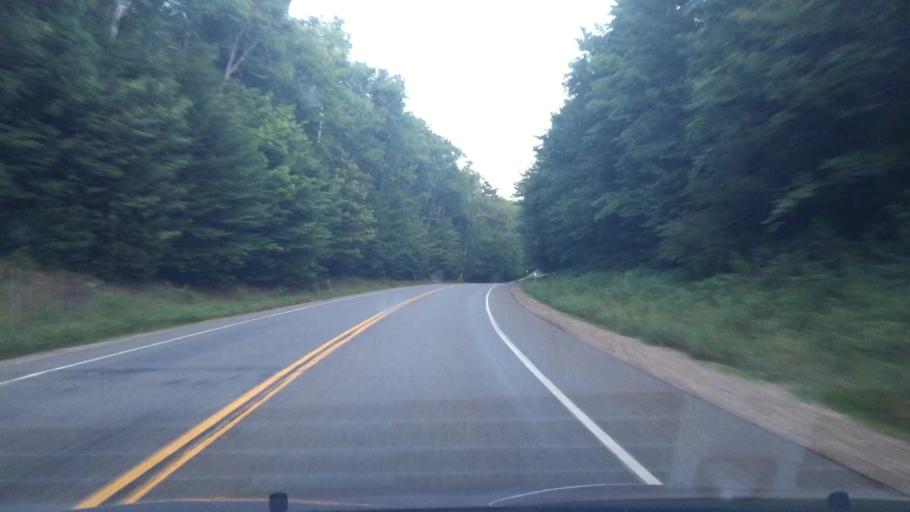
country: US
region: New Hampshire
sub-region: Grafton County
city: Woodstock
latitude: 44.0506
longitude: -71.5669
